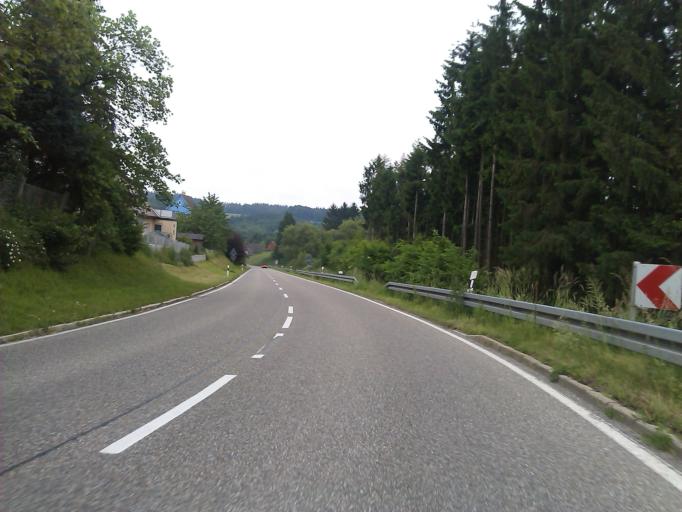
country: DE
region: Baden-Wuerttemberg
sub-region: Regierungsbezirk Stuttgart
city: Wustenrot
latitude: 49.0883
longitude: 9.4942
